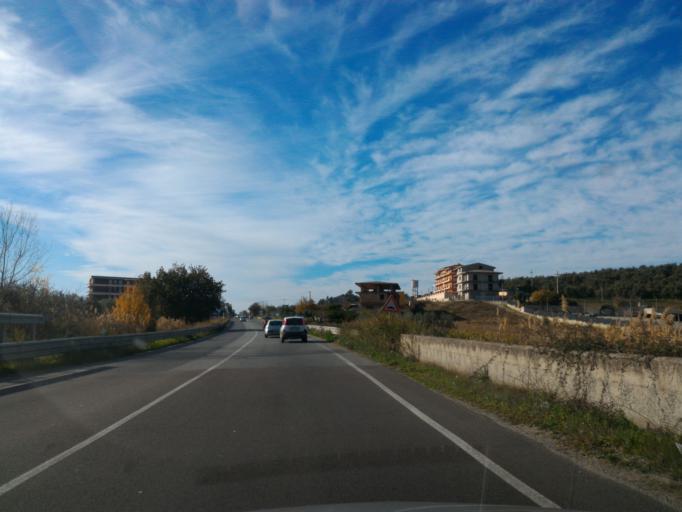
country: IT
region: Calabria
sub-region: Provincia di Catanzaro
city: Sellia Marina
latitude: 38.8929
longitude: 16.7228
